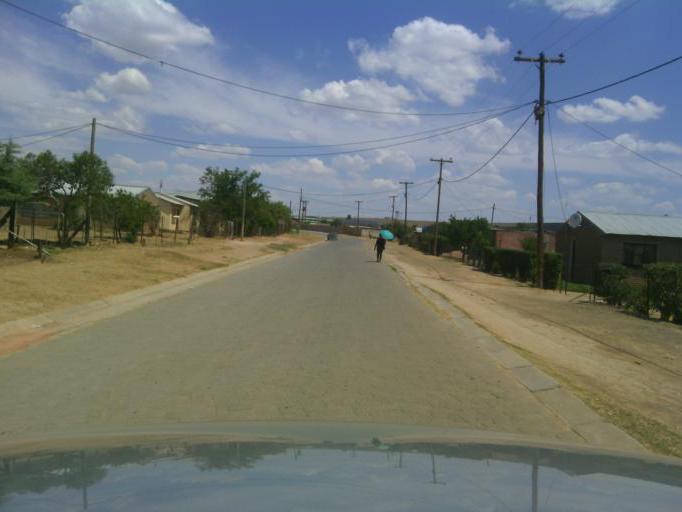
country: ZA
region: Orange Free State
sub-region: Xhariep District Municipality
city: Dewetsdorp
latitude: -29.5791
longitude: 26.6790
